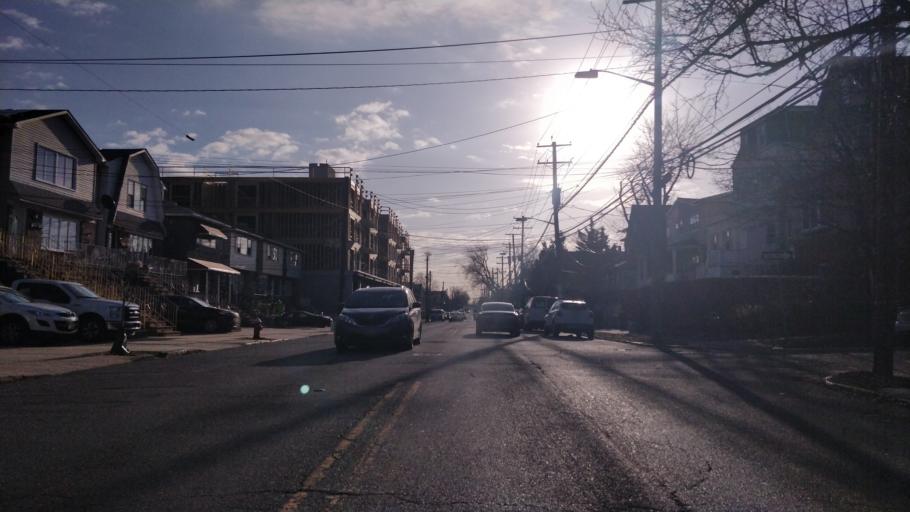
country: US
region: New Jersey
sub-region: Hudson County
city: Bayonne
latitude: 40.6782
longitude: -74.1031
